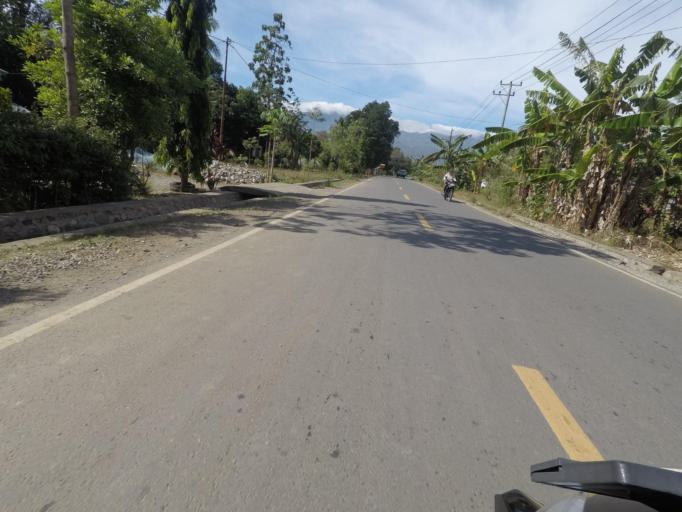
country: TL
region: Bobonaro
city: Maliana
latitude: -8.9633
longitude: 125.2164
